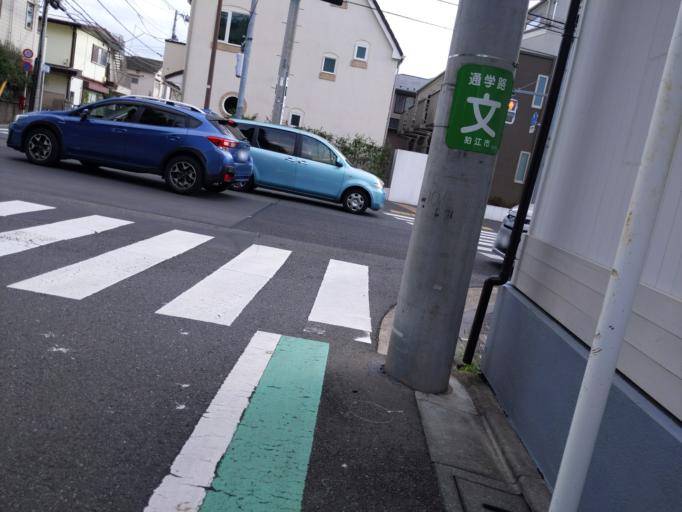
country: JP
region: Tokyo
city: Chofugaoka
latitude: 35.6378
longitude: 139.5820
